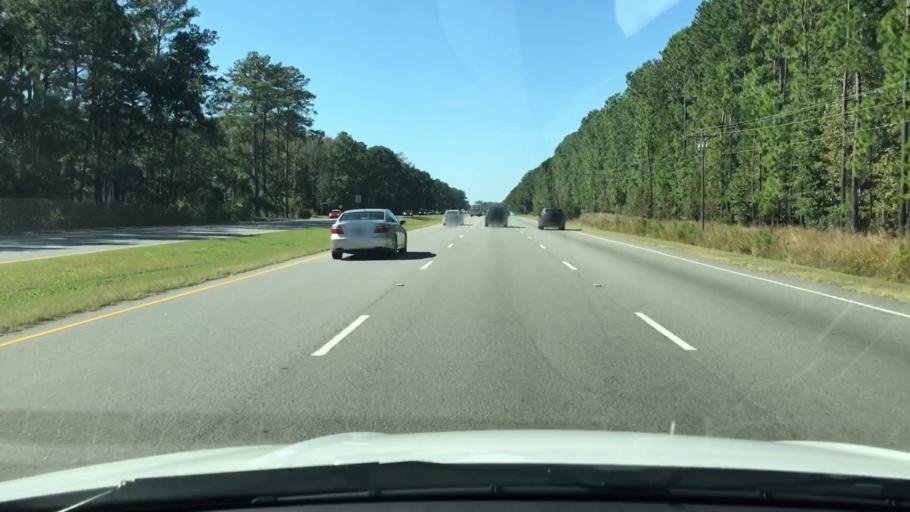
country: US
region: South Carolina
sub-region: Beaufort County
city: Bluffton
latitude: 32.2905
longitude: -80.9019
